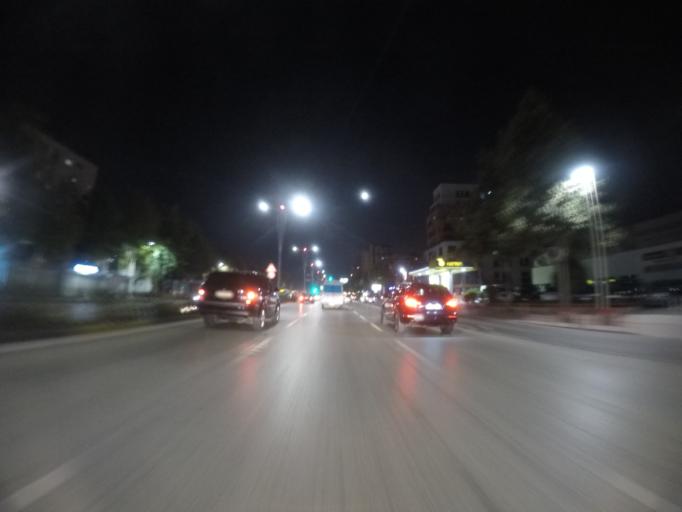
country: AL
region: Tirane
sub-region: Rrethi i Tiranes
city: Paskuqan
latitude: 41.3384
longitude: 19.7888
